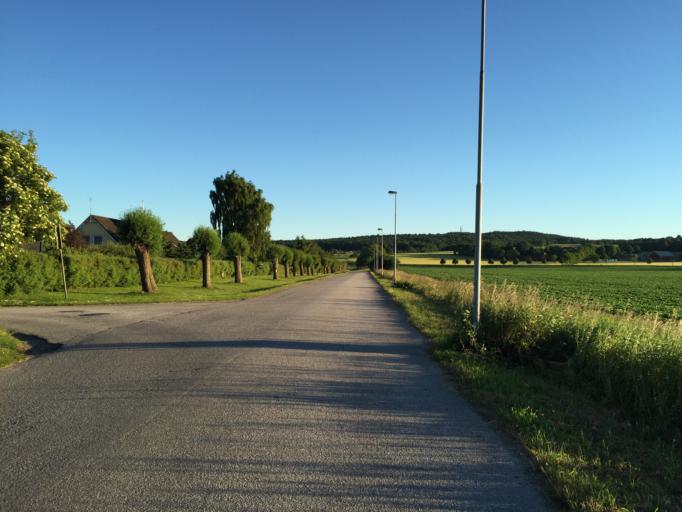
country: SE
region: Skane
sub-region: Lunds Kommun
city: Veberod
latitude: 55.6374
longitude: 13.4812
